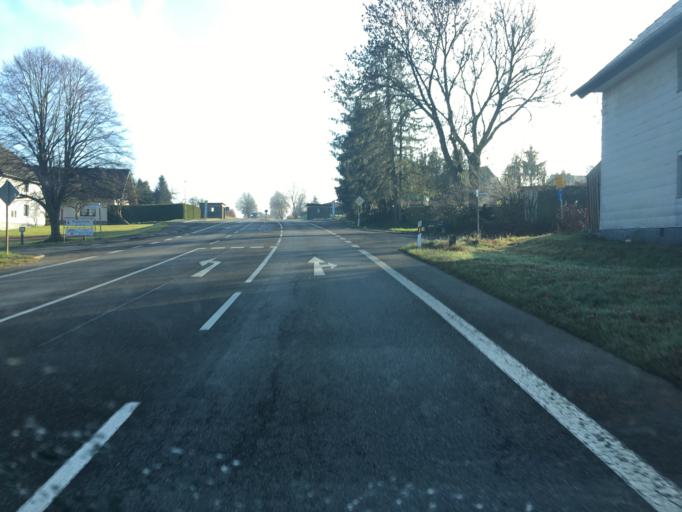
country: DE
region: North Rhine-Westphalia
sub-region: Regierungsbezirk Koln
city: Schleiden
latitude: 50.5606
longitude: 6.4436
